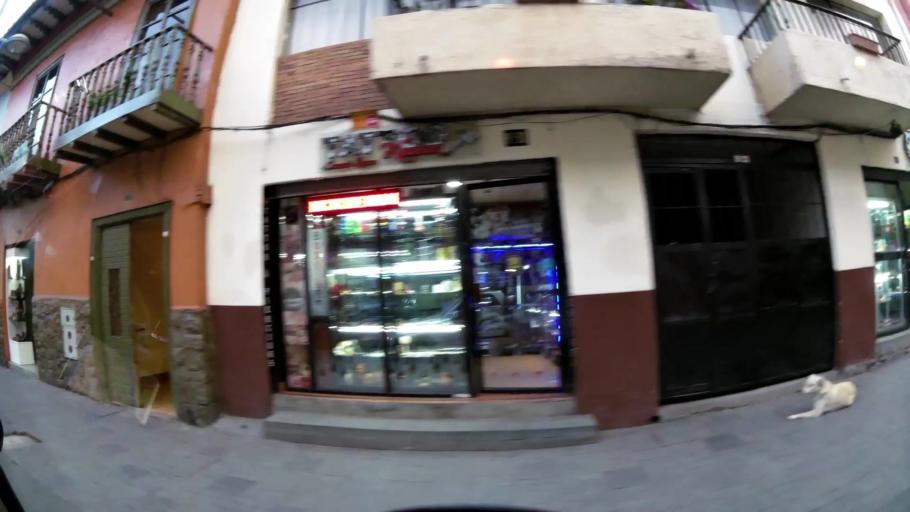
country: EC
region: Azuay
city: Cuenca
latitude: -2.9007
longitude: -79.0060
